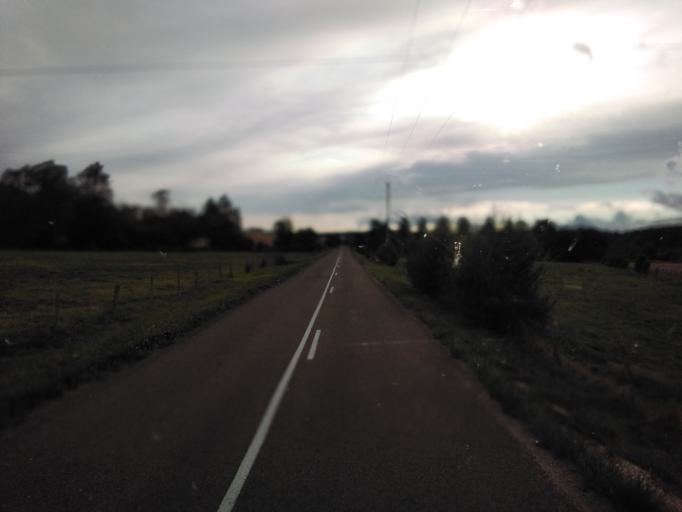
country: FR
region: Champagne-Ardenne
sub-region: Departement de l'Aube
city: Les Riceys
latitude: 47.9433
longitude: 4.3635
